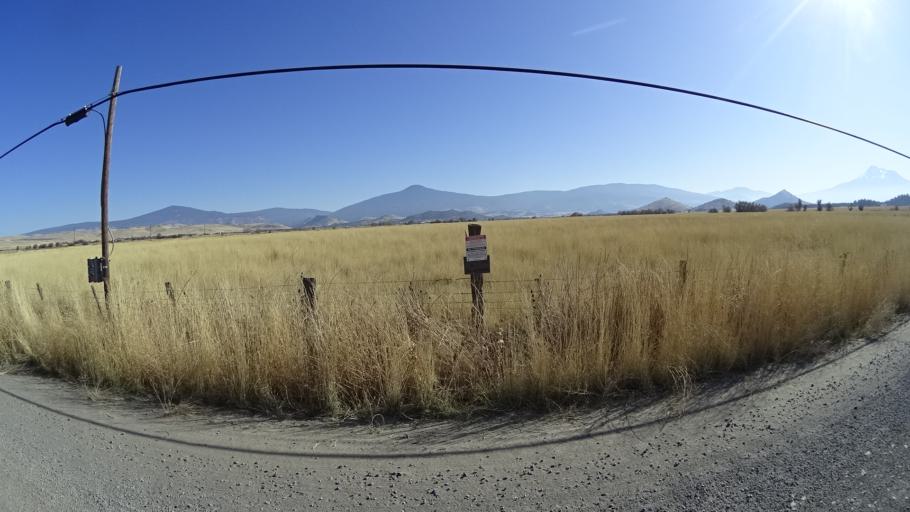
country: US
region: California
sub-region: Siskiyou County
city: Montague
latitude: 41.7092
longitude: -122.4377
